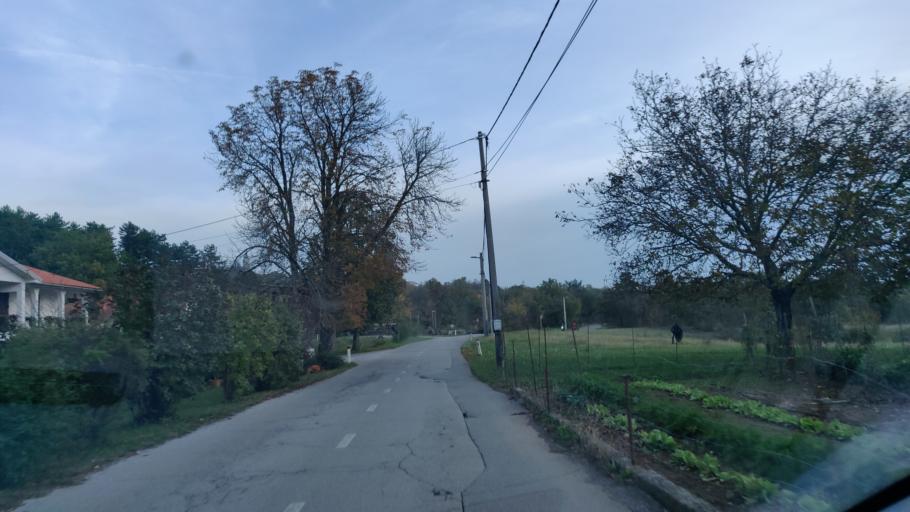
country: SI
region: Sezana
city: Sezana
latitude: 45.7849
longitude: 13.8667
